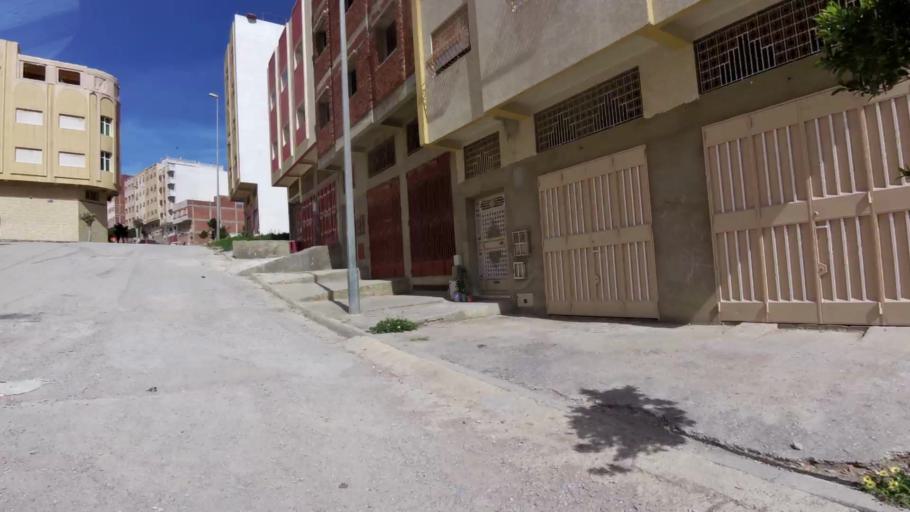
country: MA
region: Tanger-Tetouan
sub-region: Tanger-Assilah
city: Tangier
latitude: 35.7331
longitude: -5.8047
